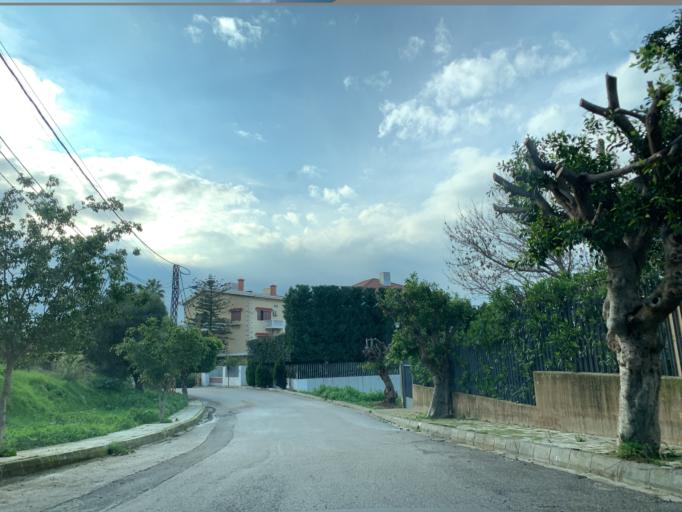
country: LB
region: Mont-Liban
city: Baabda
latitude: 33.8523
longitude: 35.5759
